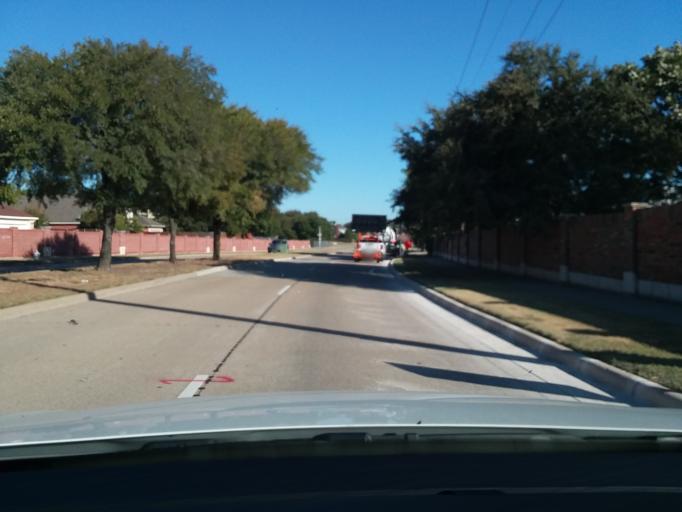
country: US
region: Texas
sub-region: Denton County
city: Lewisville
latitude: 33.0524
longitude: -97.0190
